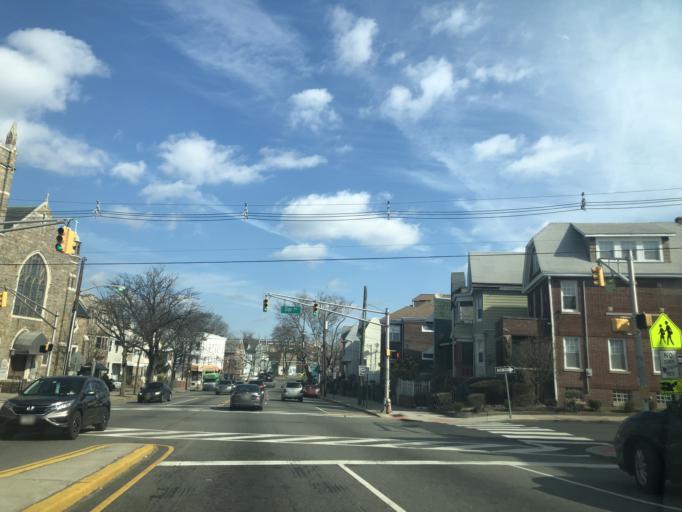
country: US
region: New Jersey
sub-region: Hudson County
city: Jersey City
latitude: 40.7139
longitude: -74.0830
